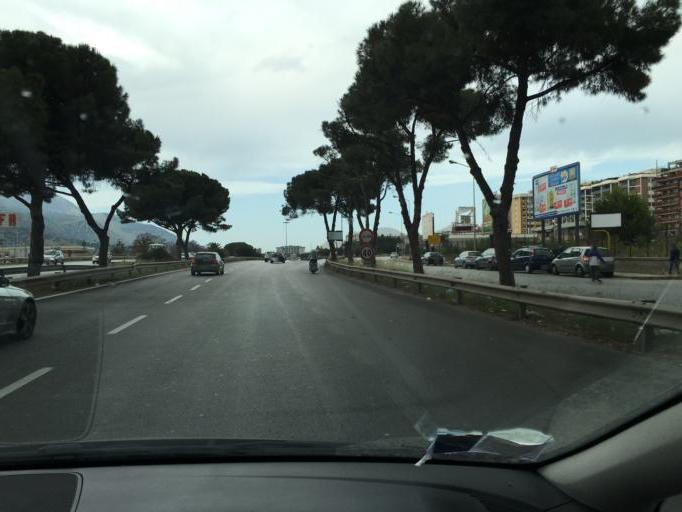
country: IT
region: Sicily
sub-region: Palermo
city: Palermo
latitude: 38.1461
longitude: 13.3286
